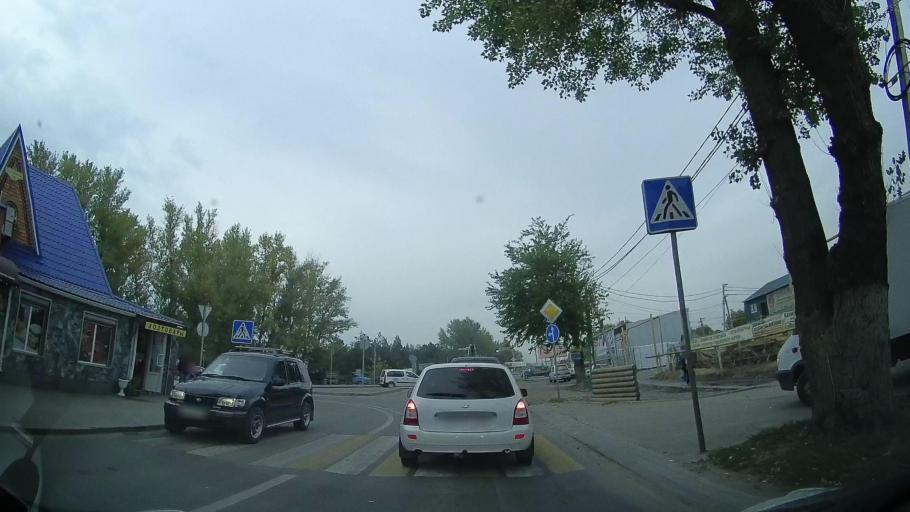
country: RU
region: Rostov
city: Severnyy
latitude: 47.2923
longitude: 39.6611
